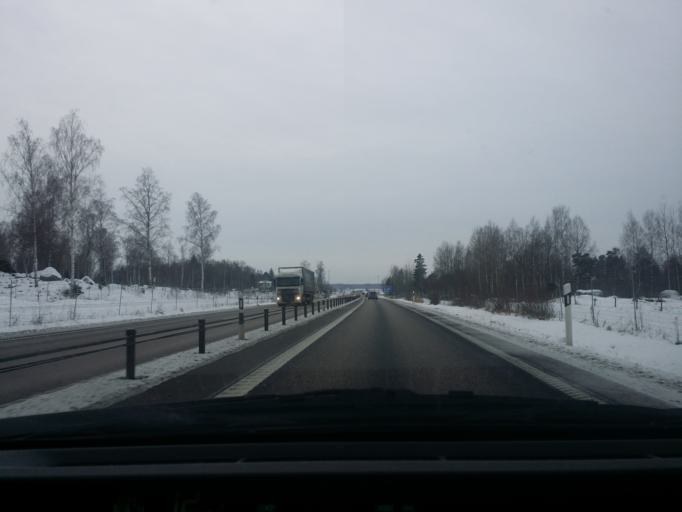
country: SE
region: Vaestra Goetaland
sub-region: Mariestads Kommun
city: Mariestad
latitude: 58.7537
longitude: 13.9608
